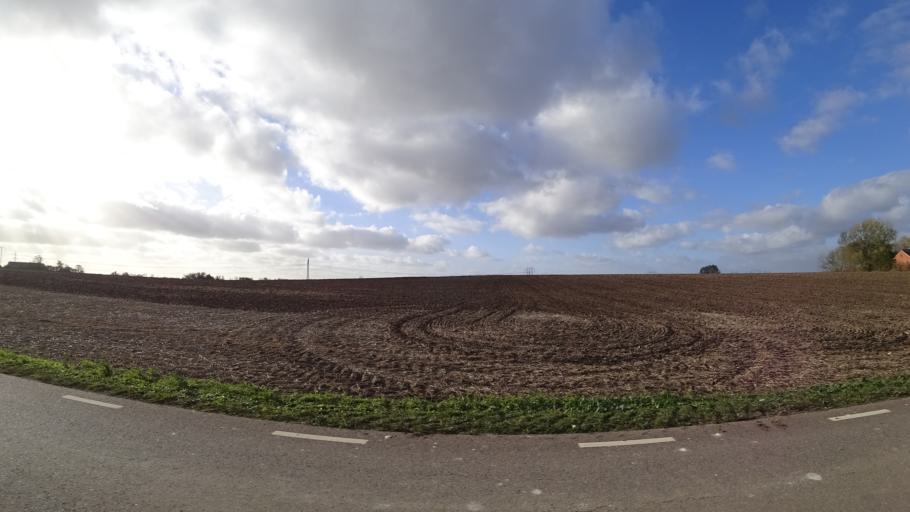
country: SE
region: Skane
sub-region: Staffanstorps Kommun
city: Hjaerup
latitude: 55.6053
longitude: 13.1409
